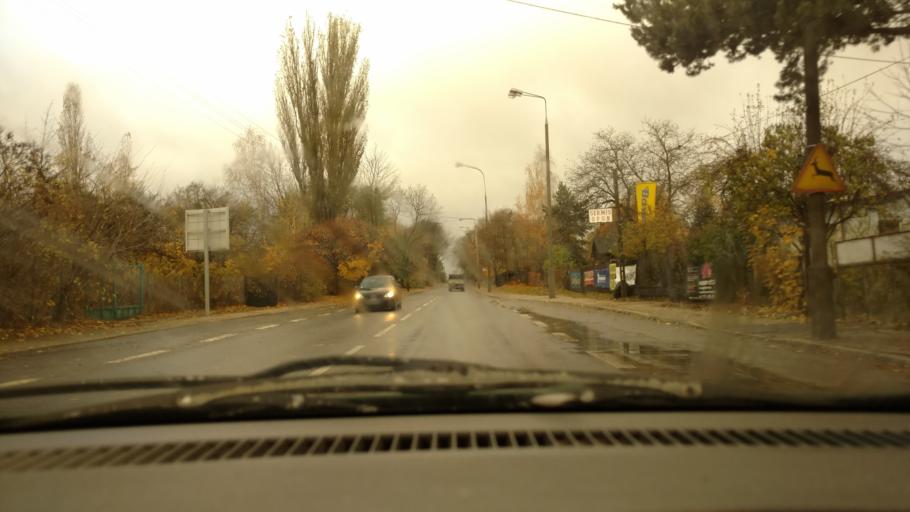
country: PL
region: Lodz Voivodeship
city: Lodz
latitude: 51.7750
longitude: 19.5209
